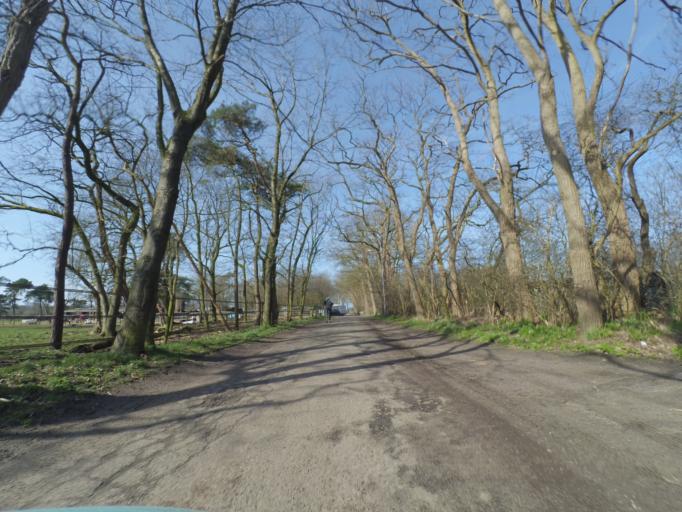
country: NL
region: Gelderland
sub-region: Gemeente Barneveld
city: Voorthuizen
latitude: 52.2065
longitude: 5.6453
